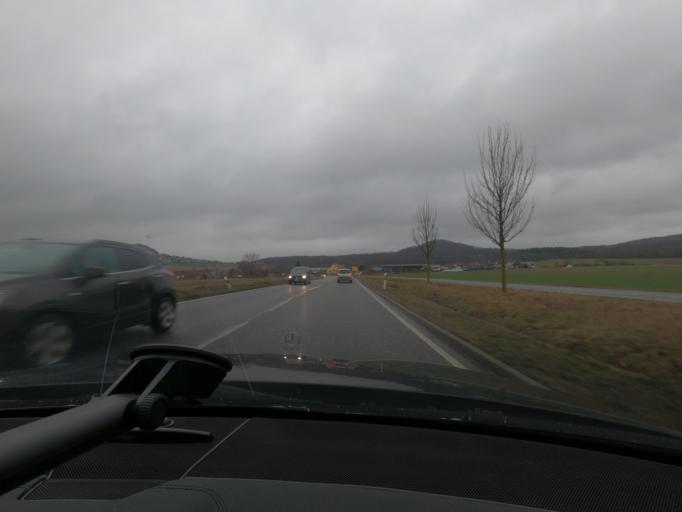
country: DE
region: Hesse
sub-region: Regierungsbezirk Kassel
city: Martinhagen
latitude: 51.3120
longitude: 9.2536
